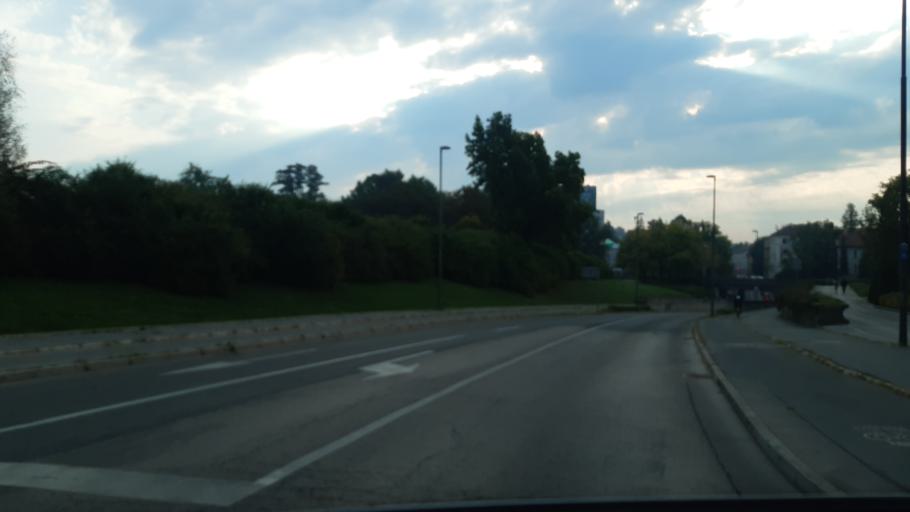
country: SI
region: Ljubljana
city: Ljubljana
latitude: 46.0515
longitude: 14.4928
